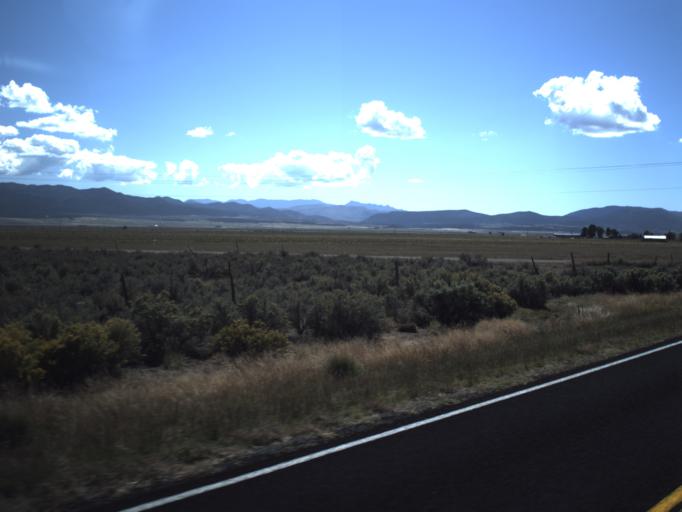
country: US
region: Utah
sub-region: Washington County
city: Enterprise
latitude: 37.6712
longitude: -113.6607
